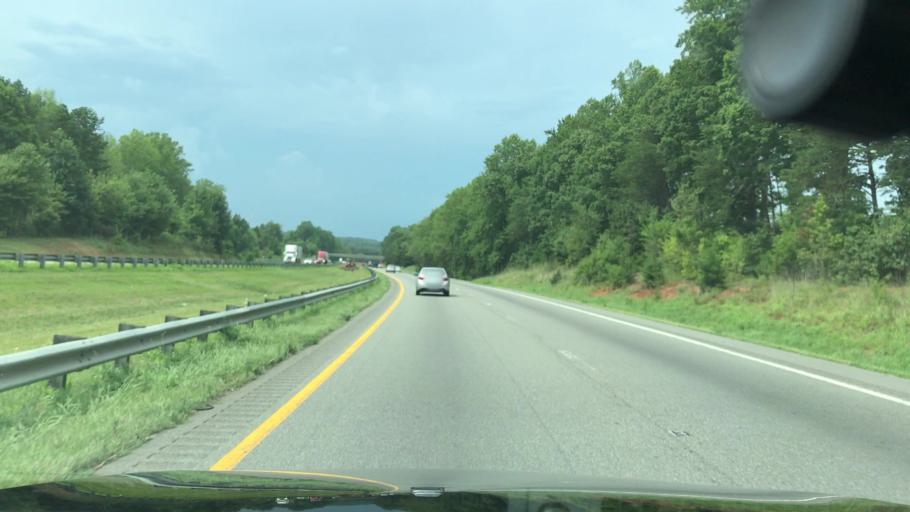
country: US
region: North Carolina
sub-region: Iredell County
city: Mooresville
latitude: 35.6184
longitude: -80.8576
